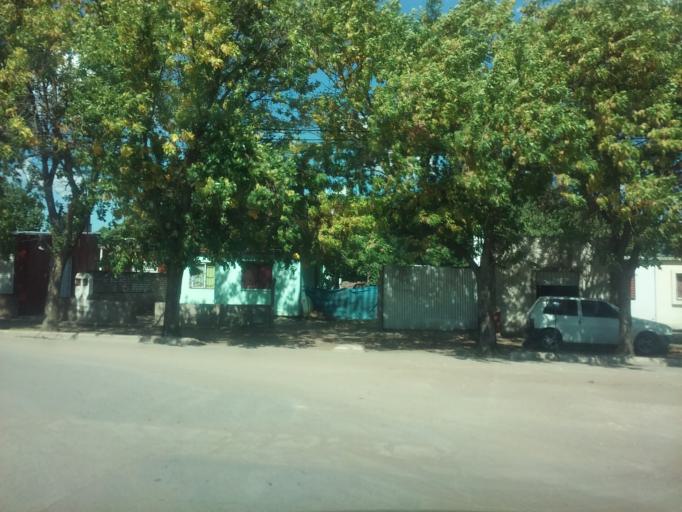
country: AR
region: La Pampa
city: Santa Rosa
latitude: -36.6444
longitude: -64.2974
